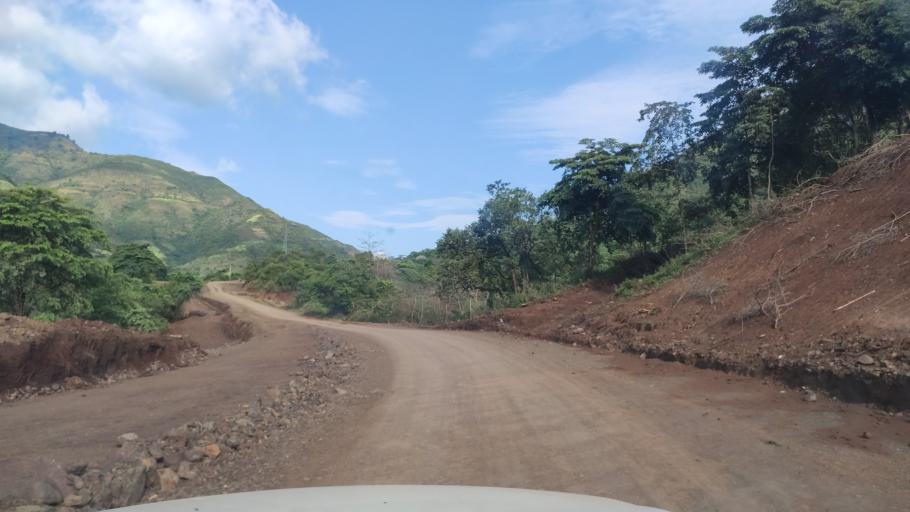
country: ET
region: Southern Nations, Nationalities, and People's Region
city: Arba Minch'
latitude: 6.4251
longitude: 37.3368
